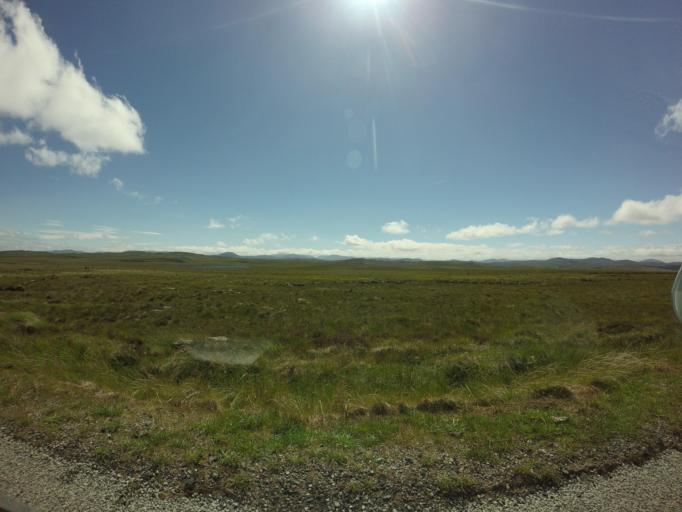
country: GB
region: Scotland
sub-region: Eilean Siar
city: Isle of Lewis
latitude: 58.1848
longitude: -6.6754
